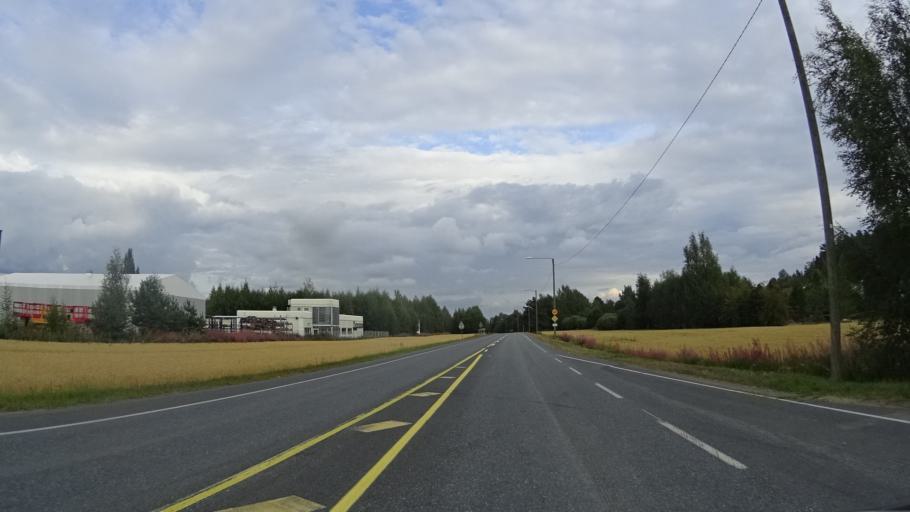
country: FI
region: Haeme
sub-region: Haemeenlinna
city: Parola
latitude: 61.0133
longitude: 24.3889
